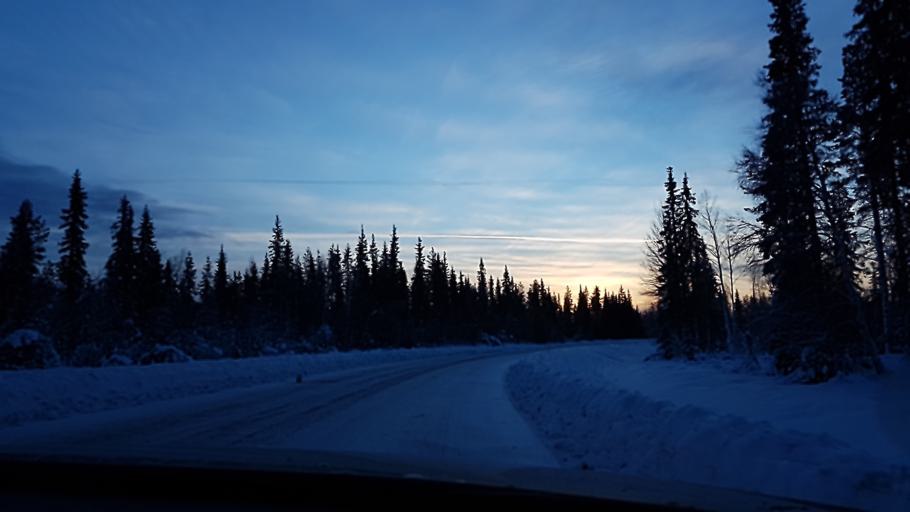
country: SE
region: Norrbotten
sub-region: Jokkmokks Kommun
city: Jokkmokk
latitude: 66.0985
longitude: 20.0696
